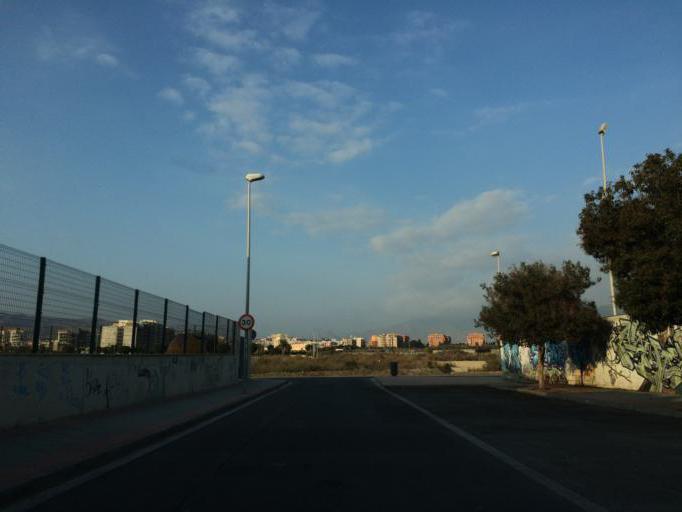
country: ES
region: Andalusia
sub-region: Provincia de Almeria
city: Almeria
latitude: 36.8260
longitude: -2.4363
